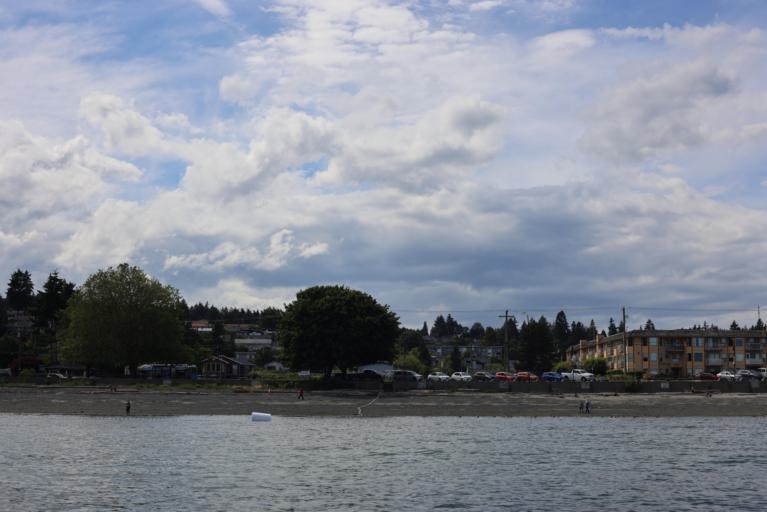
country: CA
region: British Columbia
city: Nanaimo
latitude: 49.2048
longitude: -123.9675
